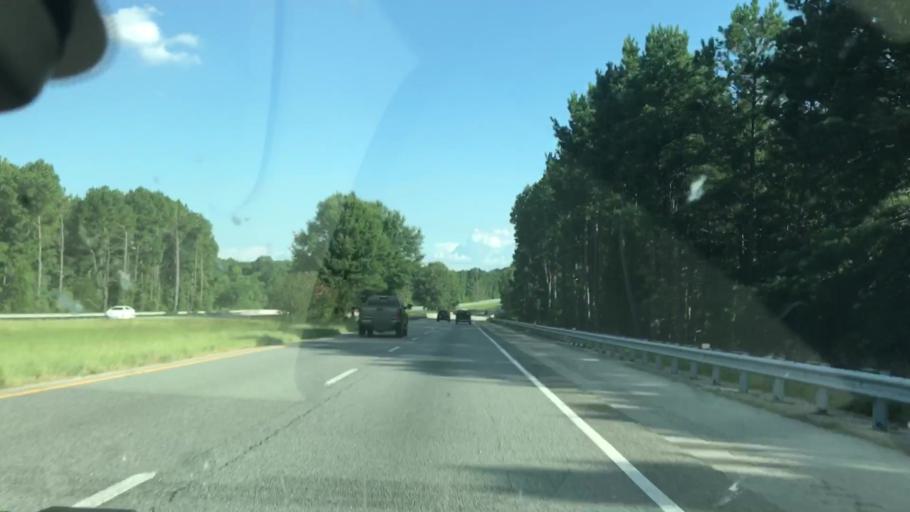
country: US
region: Georgia
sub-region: Harris County
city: Pine Mountain
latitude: 32.9337
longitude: -84.9515
